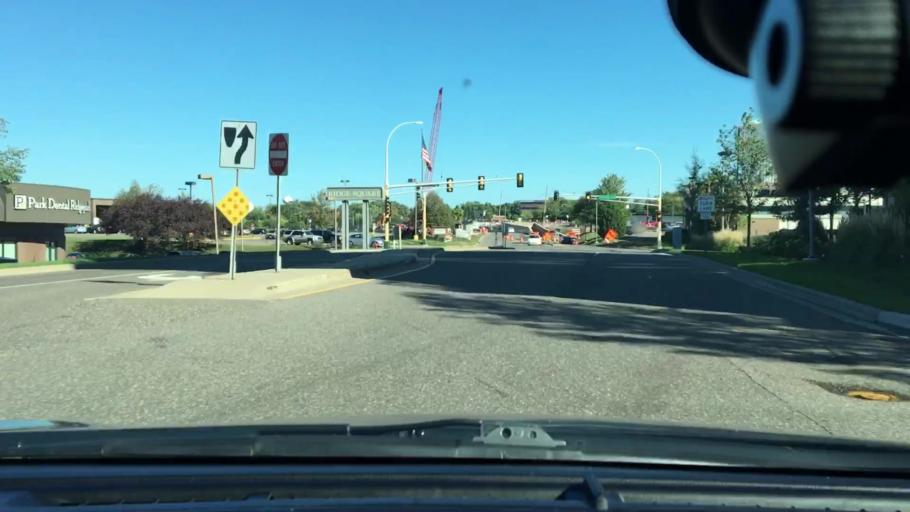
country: US
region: Minnesota
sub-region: Hennepin County
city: Minnetonka Mills
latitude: 44.9669
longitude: -93.4441
